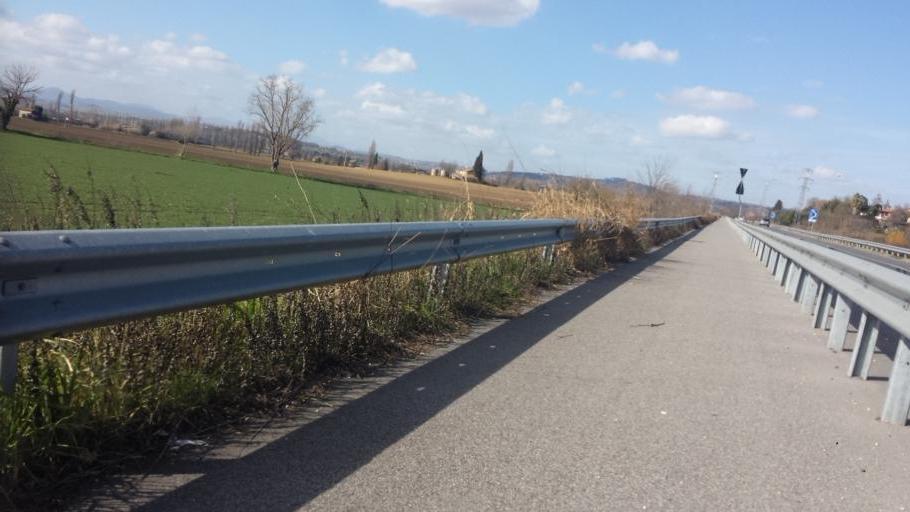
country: IT
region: Umbria
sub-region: Provincia di Terni
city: Terni
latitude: 42.5727
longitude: 12.6008
